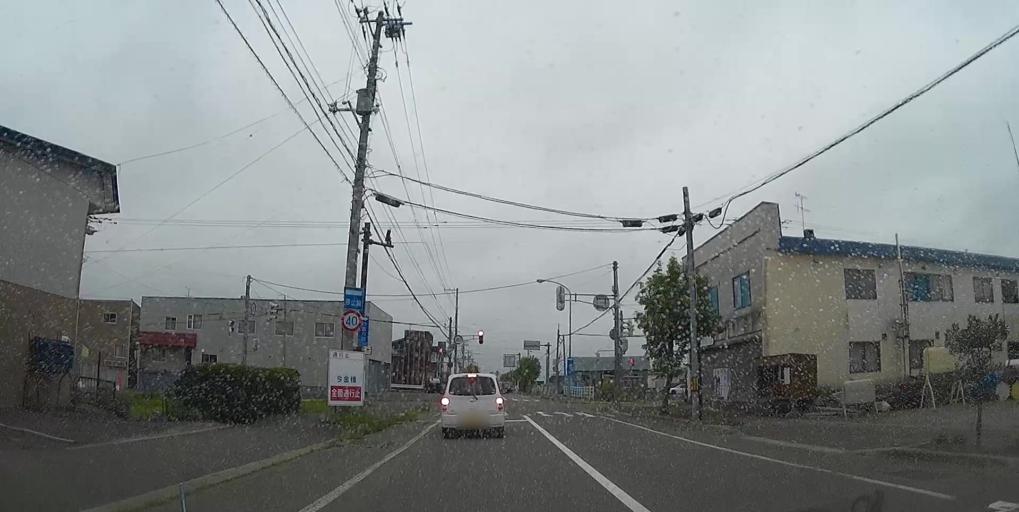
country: JP
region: Hokkaido
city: Iwanai
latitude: 42.4267
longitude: 140.0083
